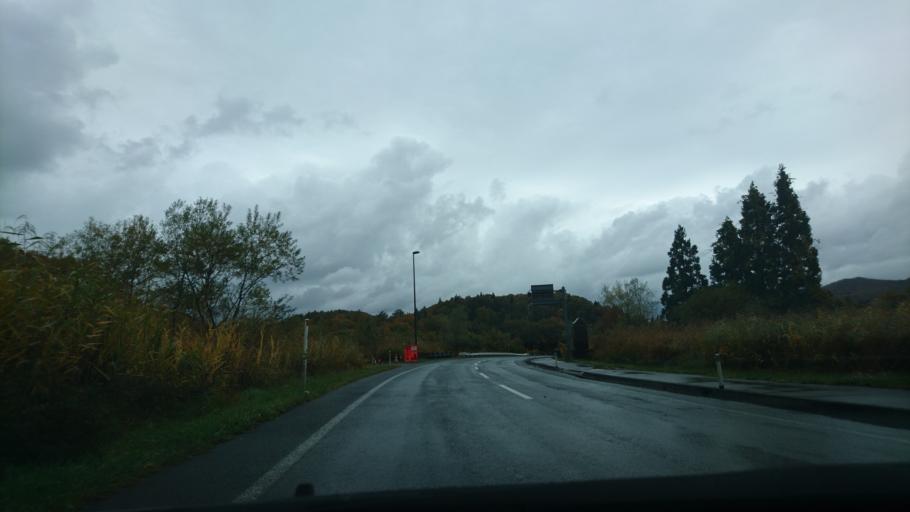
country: JP
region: Akita
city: Yokotemachi
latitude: 39.3576
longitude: 140.7615
